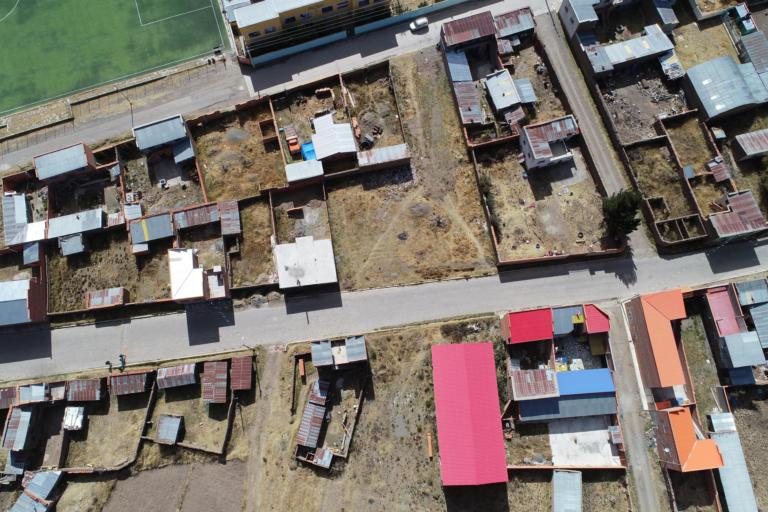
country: BO
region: La Paz
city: Achacachi
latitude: -15.8966
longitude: -68.9080
